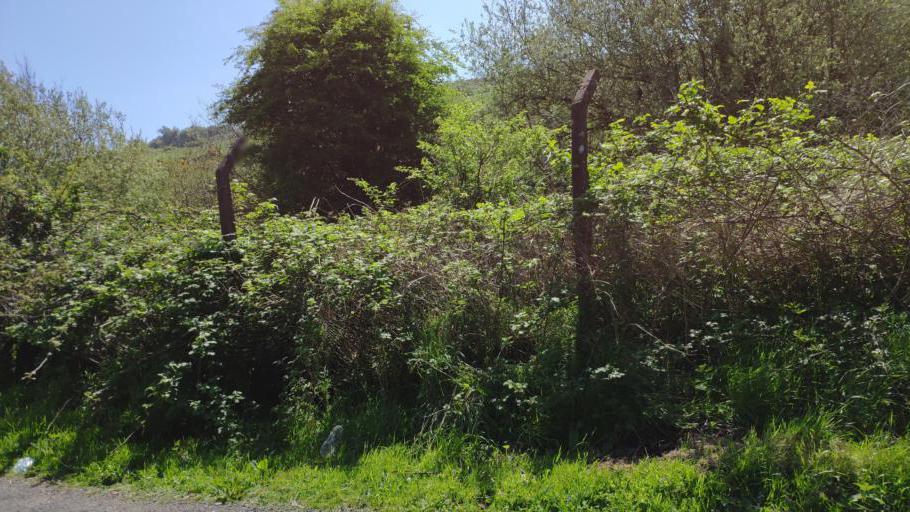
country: IE
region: Munster
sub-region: County Cork
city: Cork
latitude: 51.9176
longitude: -8.5076
